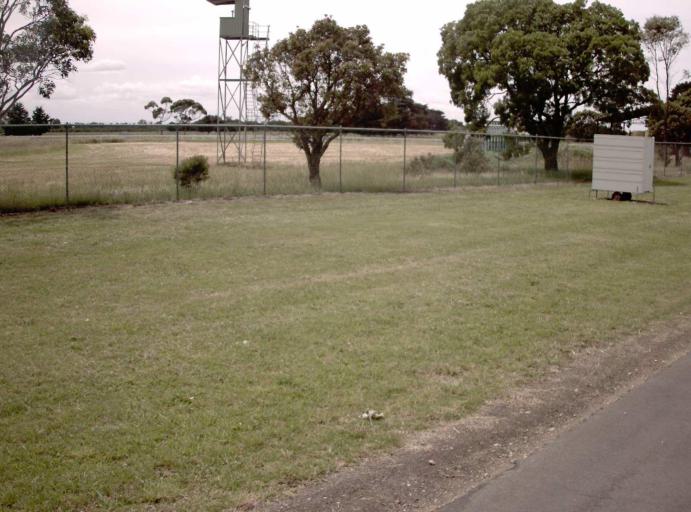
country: AU
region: Victoria
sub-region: Wellington
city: Sale
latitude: -38.0754
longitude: 147.0439
